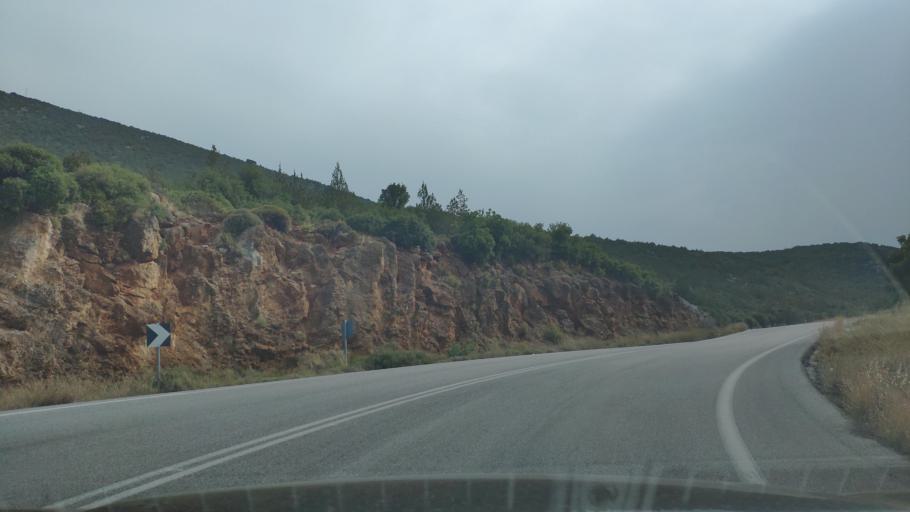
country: GR
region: Peloponnese
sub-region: Nomos Argolidos
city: Didyma
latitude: 37.5108
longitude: 23.2000
